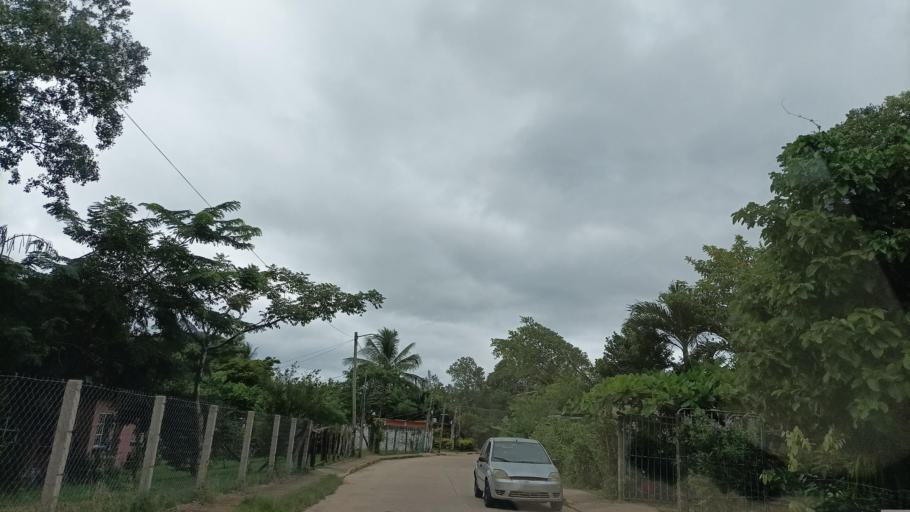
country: MX
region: Veracruz
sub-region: Cosoleacaque
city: Residencial las Olas
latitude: 18.0684
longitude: -94.5903
